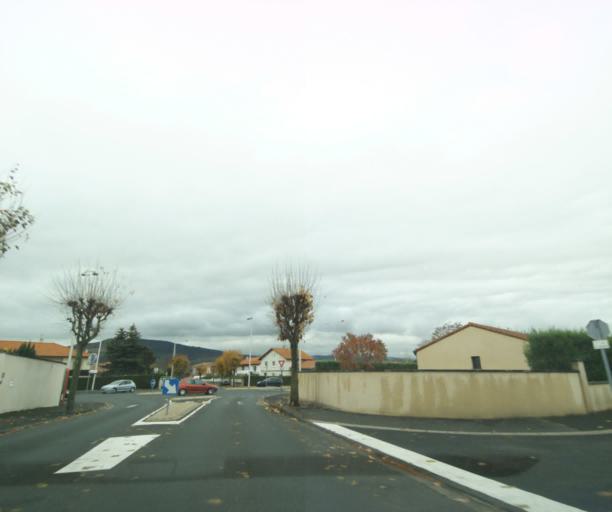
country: FR
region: Auvergne
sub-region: Departement du Puy-de-Dome
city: Cournon-d'Auvergne
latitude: 45.7381
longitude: 3.1777
